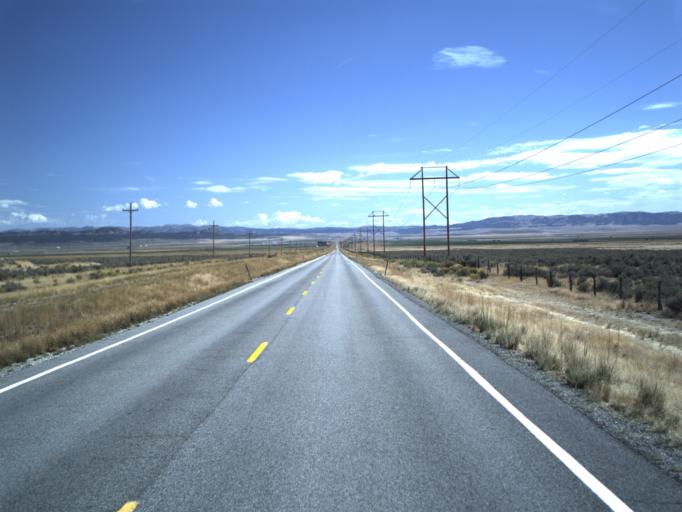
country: US
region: Idaho
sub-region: Oneida County
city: Malad City
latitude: 41.9660
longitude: -112.9799
